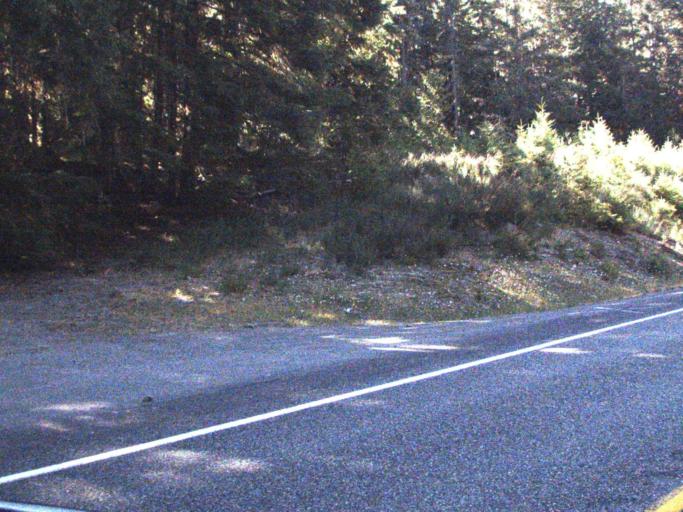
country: US
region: Washington
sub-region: King County
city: Enumclaw
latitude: 46.9987
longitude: -121.5290
